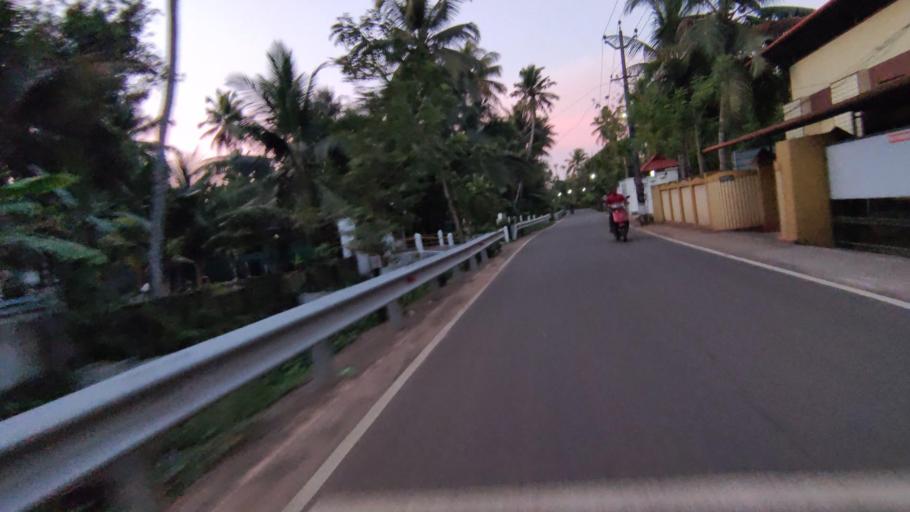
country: IN
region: Kerala
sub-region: Kottayam
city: Kottayam
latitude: 9.5831
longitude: 76.4361
